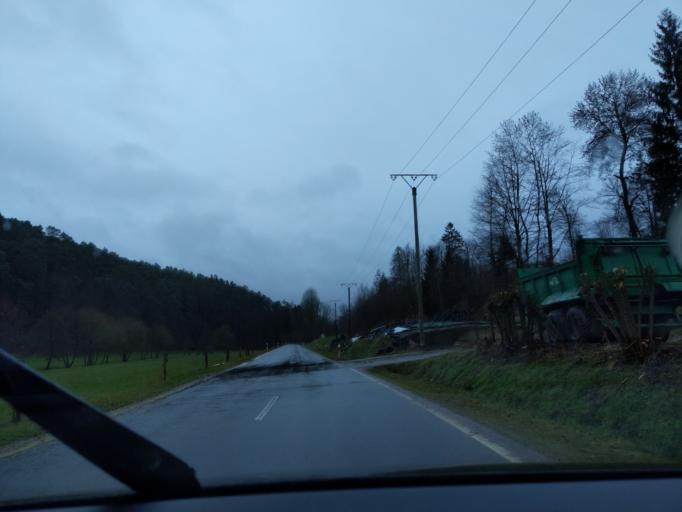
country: DE
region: Hesse
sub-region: Regierungsbezirk Kassel
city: Bad Arolsen
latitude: 51.3348
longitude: 9.0713
